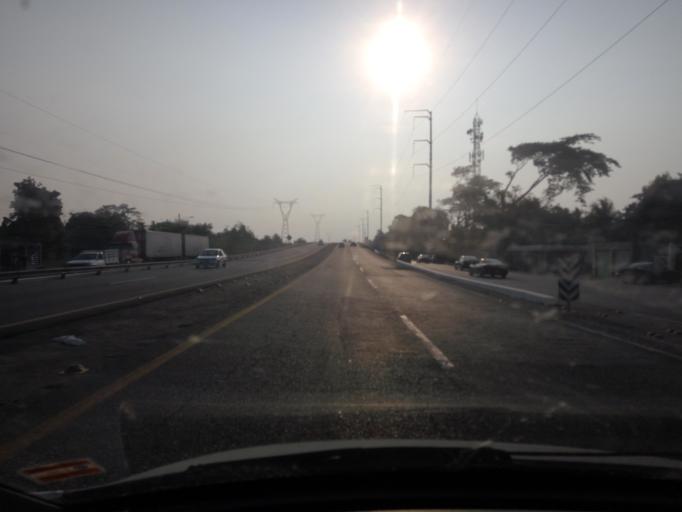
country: MX
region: Tabasco
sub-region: Cunduacan
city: Cumuapa 1ra. Seccion
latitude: 17.9740
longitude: -93.1255
